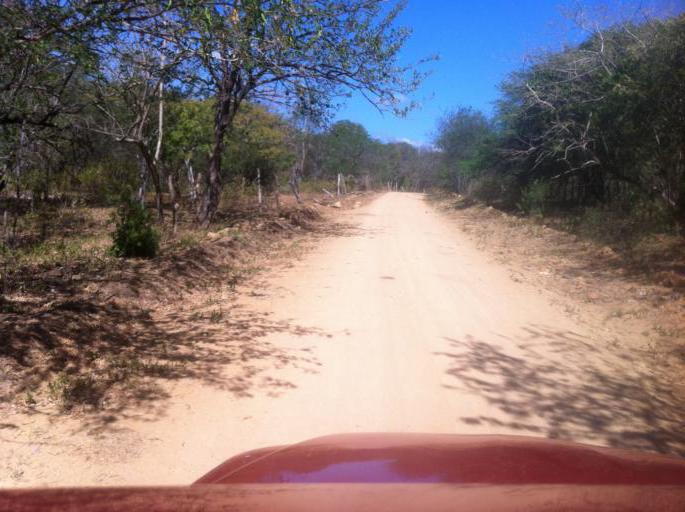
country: NI
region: Carazo
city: Santa Teresa
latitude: 11.6183
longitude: -86.3195
